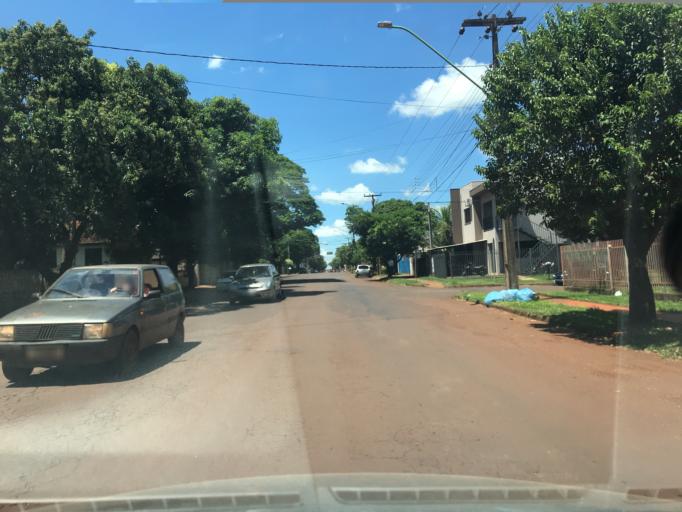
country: BR
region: Parana
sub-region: Palotina
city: Palotina
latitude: -24.2894
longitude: -53.8455
